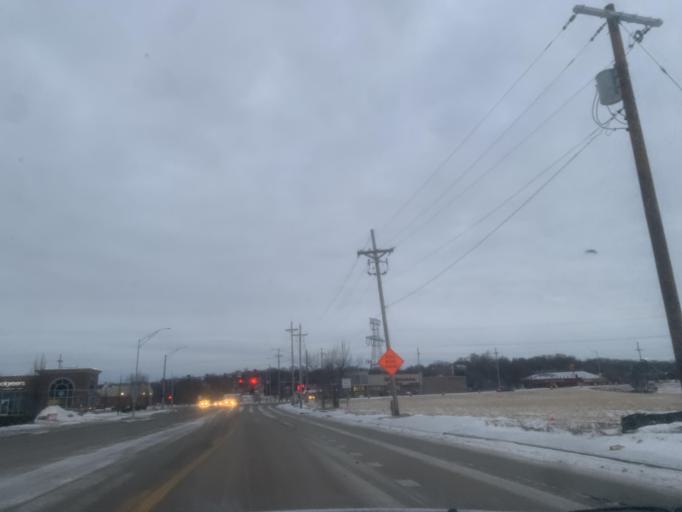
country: US
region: Nebraska
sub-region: Douglas County
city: Ralston
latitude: 41.2355
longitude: -96.0526
